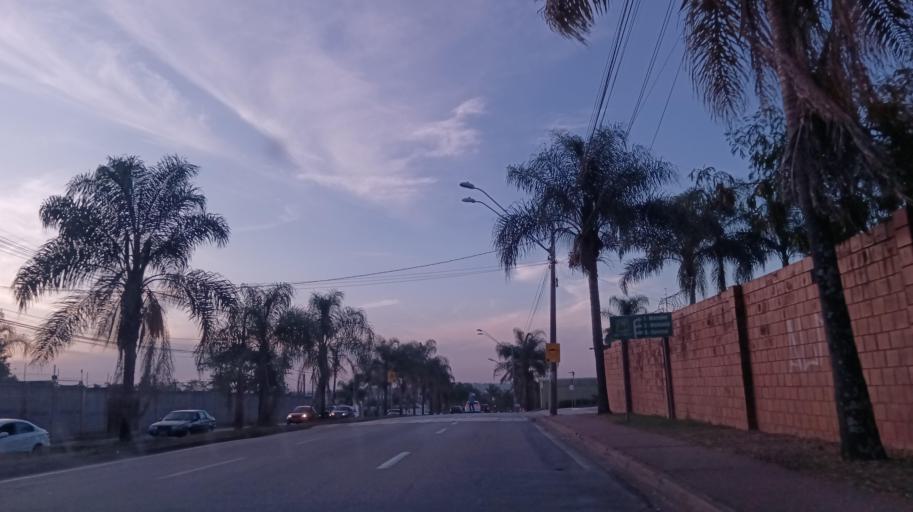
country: BR
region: Sao Paulo
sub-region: Sorocaba
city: Sorocaba
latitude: -23.4463
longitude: -47.5048
